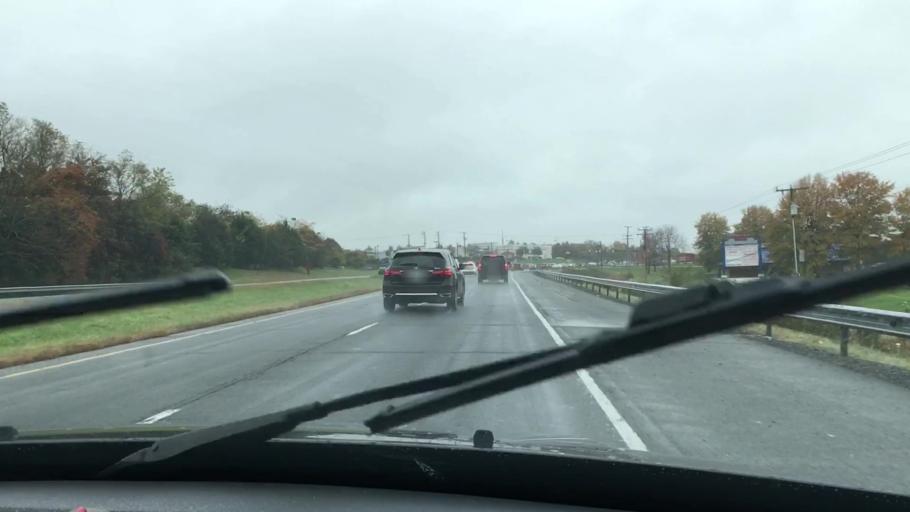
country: US
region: Virginia
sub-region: Loudoun County
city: Leesburg
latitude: 39.1163
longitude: -77.5389
